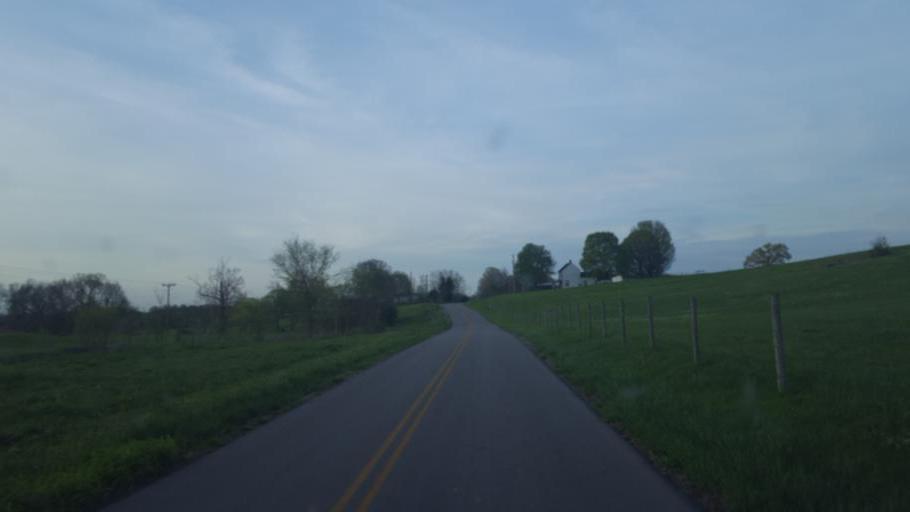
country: US
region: Kentucky
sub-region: Metcalfe County
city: Edmonton
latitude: 37.0504
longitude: -85.7056
